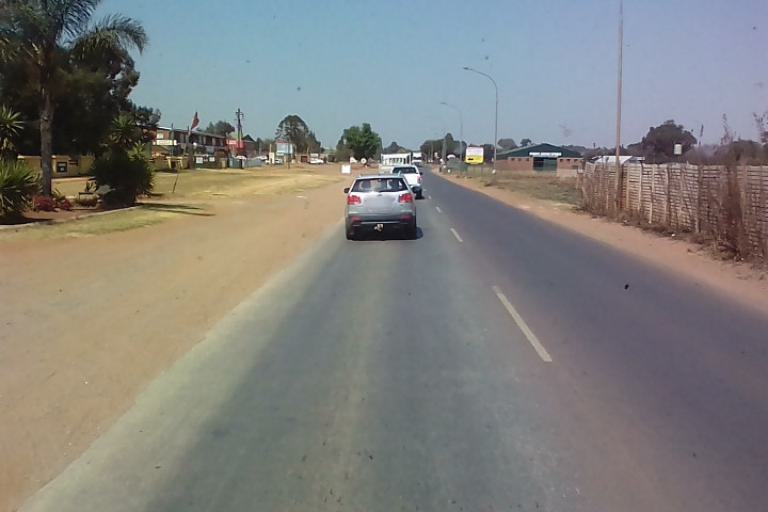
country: ZA
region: Gauteng
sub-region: Ekurhuleni Metropolitan Municipality
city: Benoni
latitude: -26.1065
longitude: 28.2961
